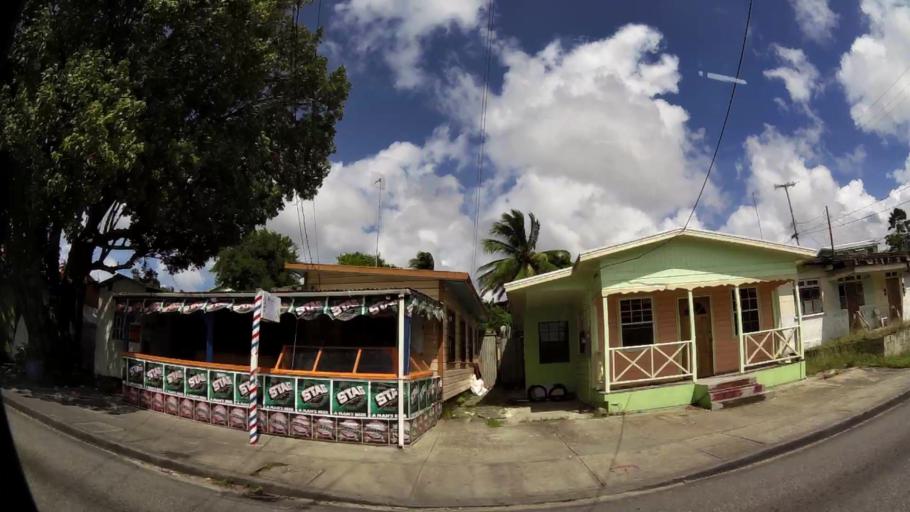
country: BB
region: Saint Michael
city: Bridgetown
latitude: 13.1291
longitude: -59.6304
